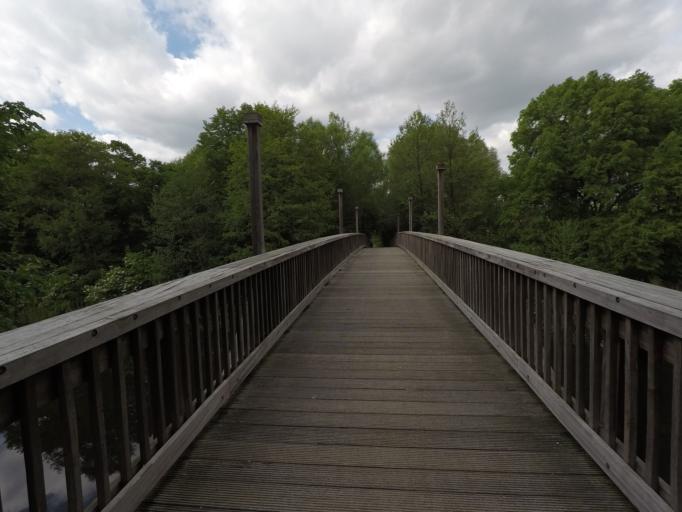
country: DE
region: Brandenburg
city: Melchow
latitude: 52.8453
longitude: 13.6959
